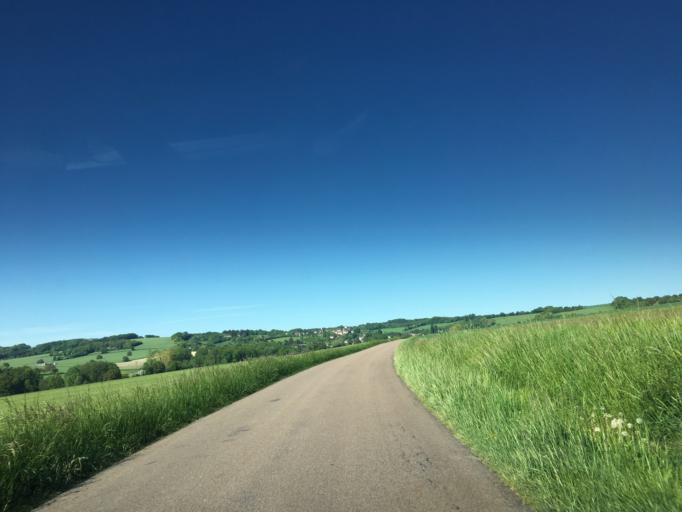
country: FR
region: Bourgogne
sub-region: Departement de l'Yonne
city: Aillant-sur-Tholon
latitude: 47.8261
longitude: 3.3303
